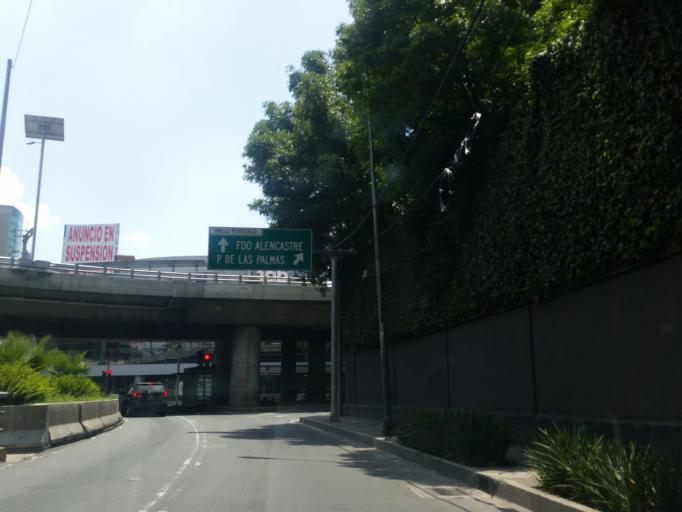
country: MX
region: Mexico City
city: Miguel Hidalgo
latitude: 19.4317
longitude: -99.2092
